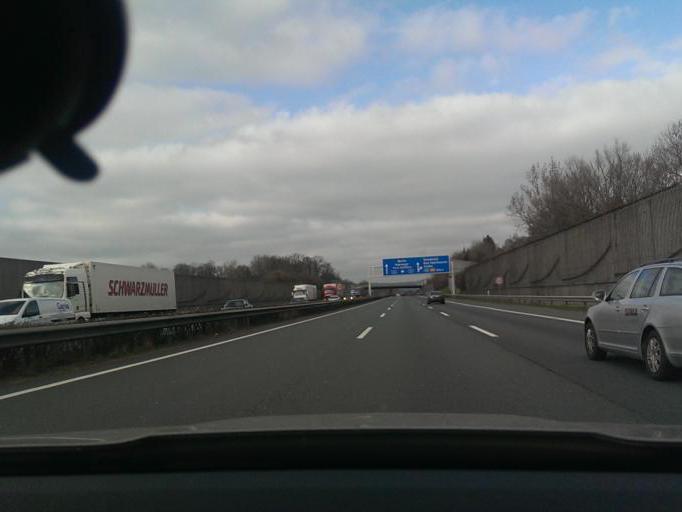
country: DE
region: North Rhine-Westphalia
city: Bad Oeynhausen
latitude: 52.1953
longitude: 8.8285
